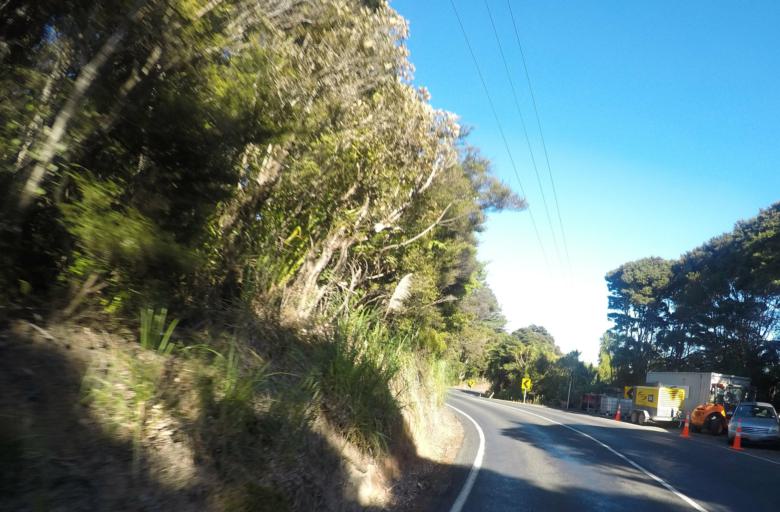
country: NZ
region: Auckland
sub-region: Auckland
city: Titirangi
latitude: -36.9675
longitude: 174.5005
